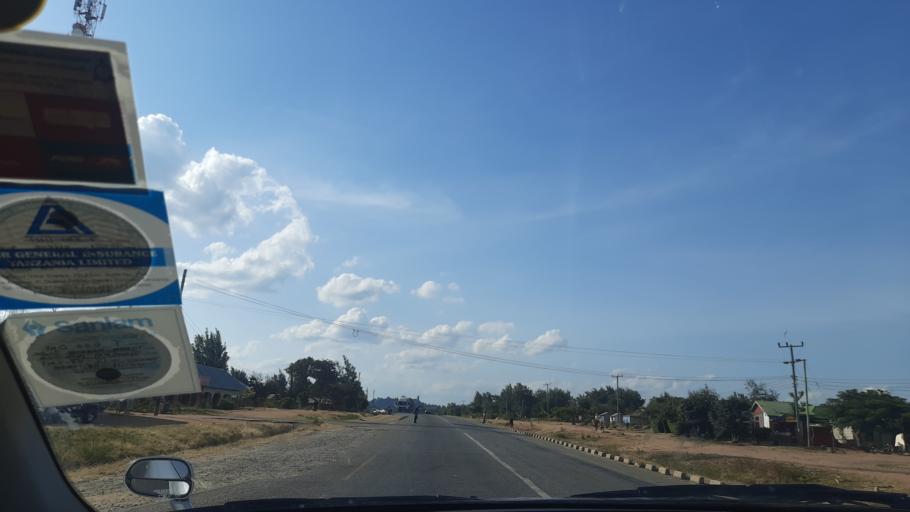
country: TZ
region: Singida
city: Puma
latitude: -5.0037
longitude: 34.7575
